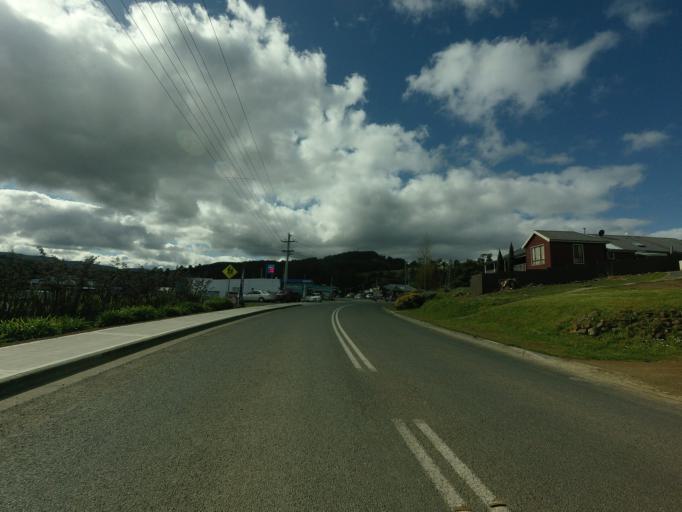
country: AU
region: Tasmania
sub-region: Huon Valley
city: Geeveston
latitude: -43.1653
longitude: 146.9263
